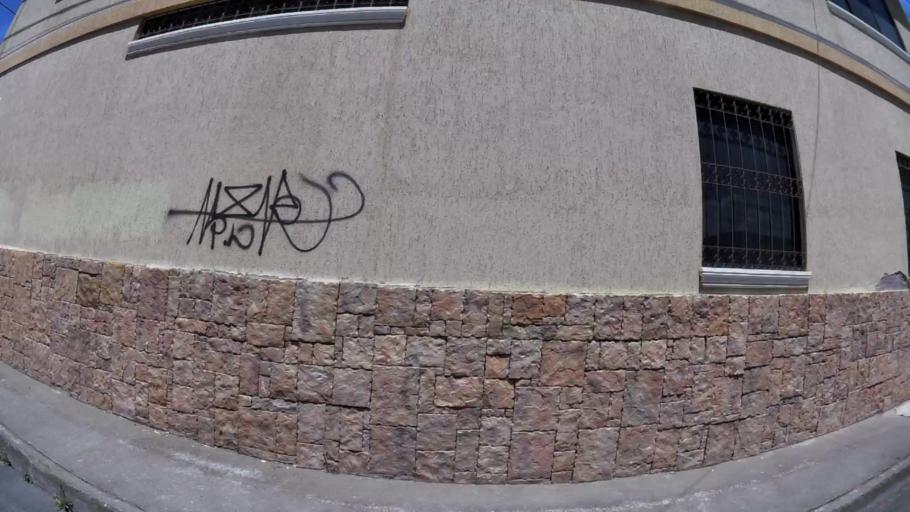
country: EC
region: Chimborazo
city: Riobamba
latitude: -1.6604
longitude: -78.6582
